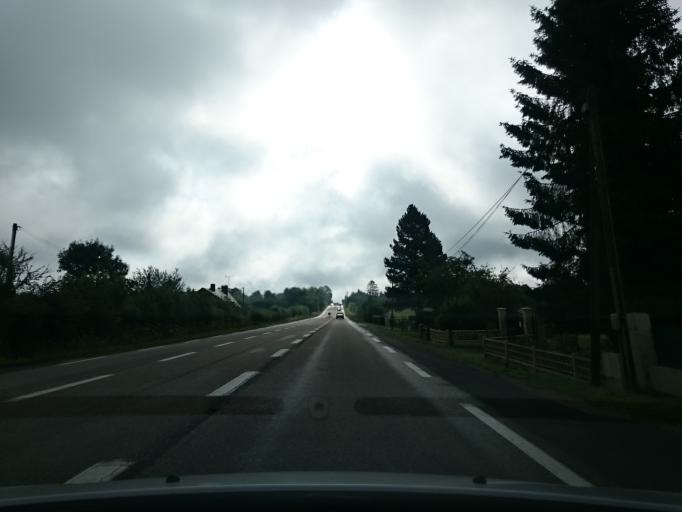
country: FR
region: Lower Normandy
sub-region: Departement du Calvados
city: Saint-Desir
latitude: 49.1354
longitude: 0.1367
